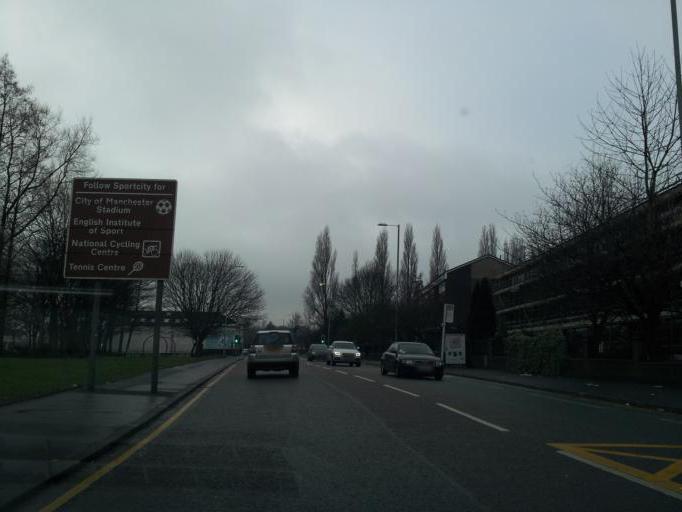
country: GB
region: England
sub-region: Manchester
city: Blackley
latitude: 53.5077
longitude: -2.2174
